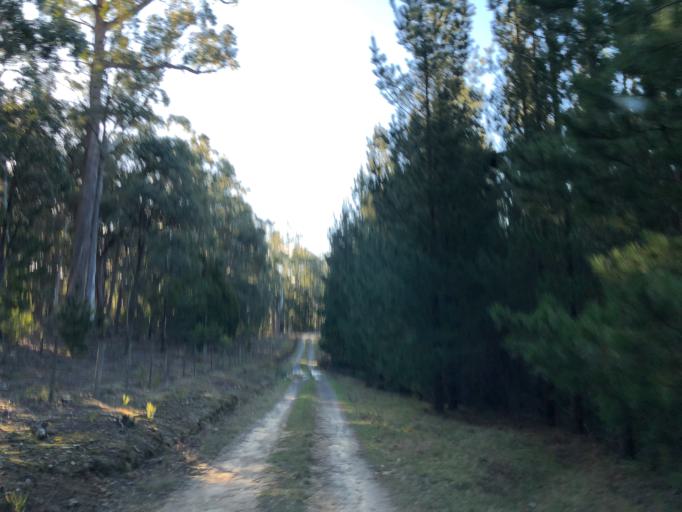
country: AU
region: Victoria
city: Brown Hill
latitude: -37.5055
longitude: 144.1512
